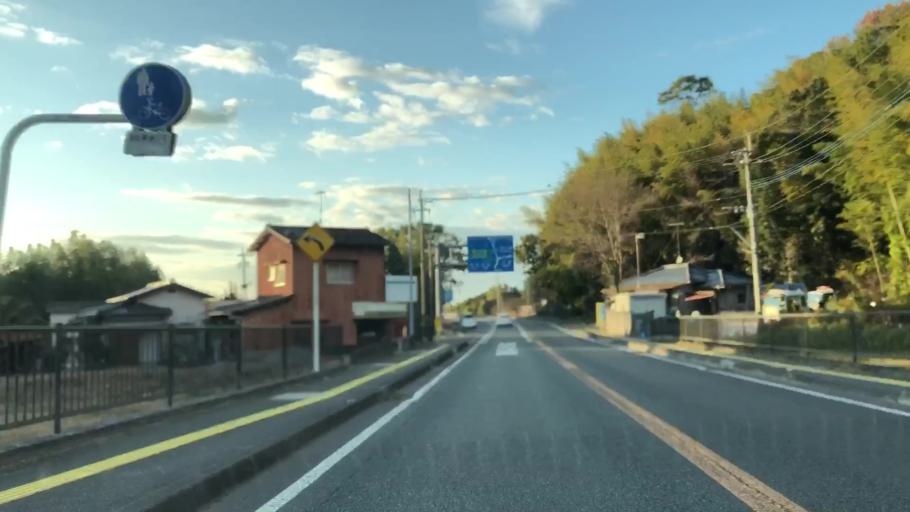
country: JP
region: Fukuoka
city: Nakatsu
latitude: 33.5381
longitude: 131.2997
